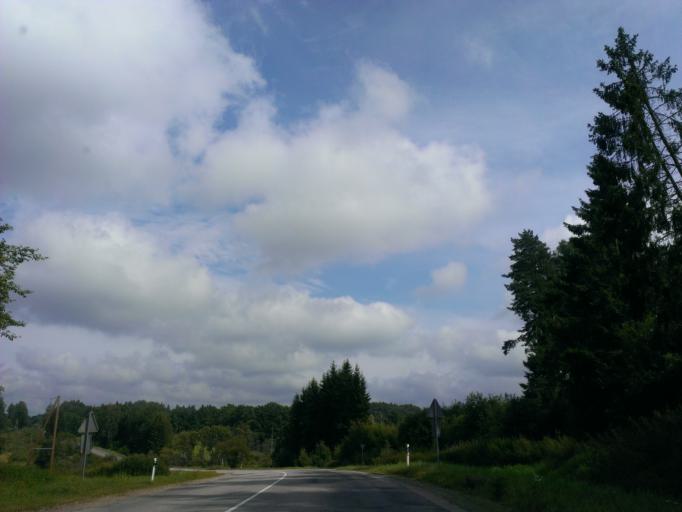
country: LV
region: Amatas Novads
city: Drabesi
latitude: 57.2411
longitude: 25.3073
